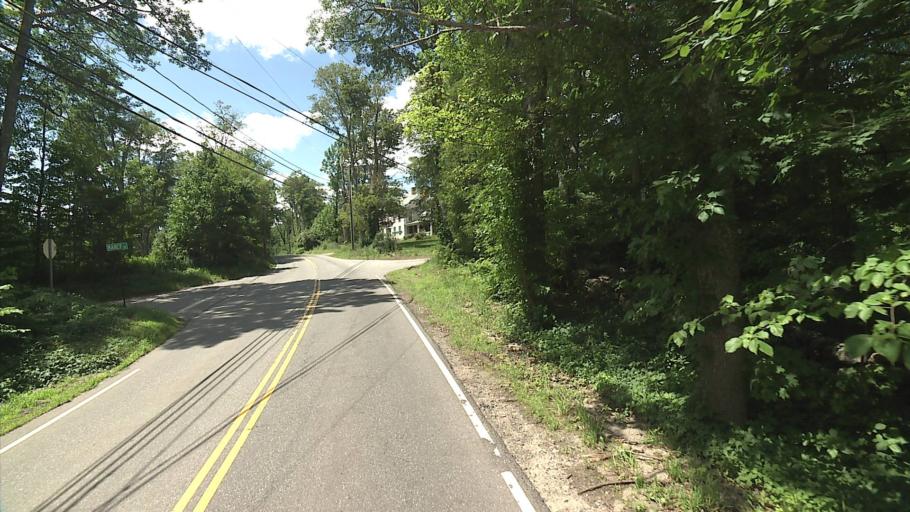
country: US
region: Connecticut
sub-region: Windham County
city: South Woodstock
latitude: 41.9715
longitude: -72.0607
